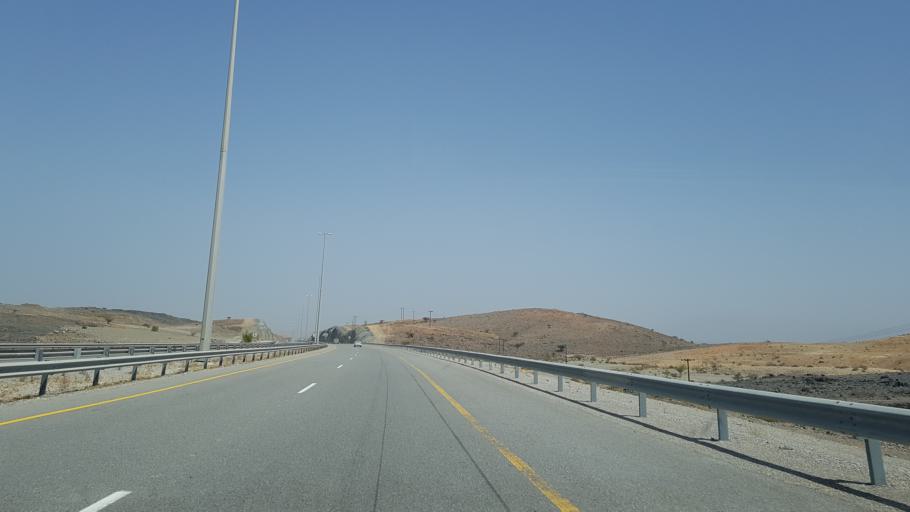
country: OM
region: Muhafazat Masqat
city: Muscat
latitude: 23.1925
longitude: 58.8393
